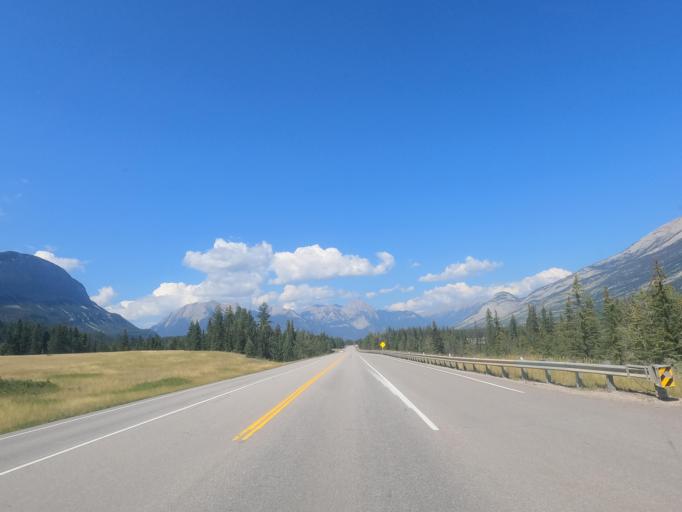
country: CA
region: Alberta
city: Jasper Park Lodge
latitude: 52.9627
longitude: -118.0509
